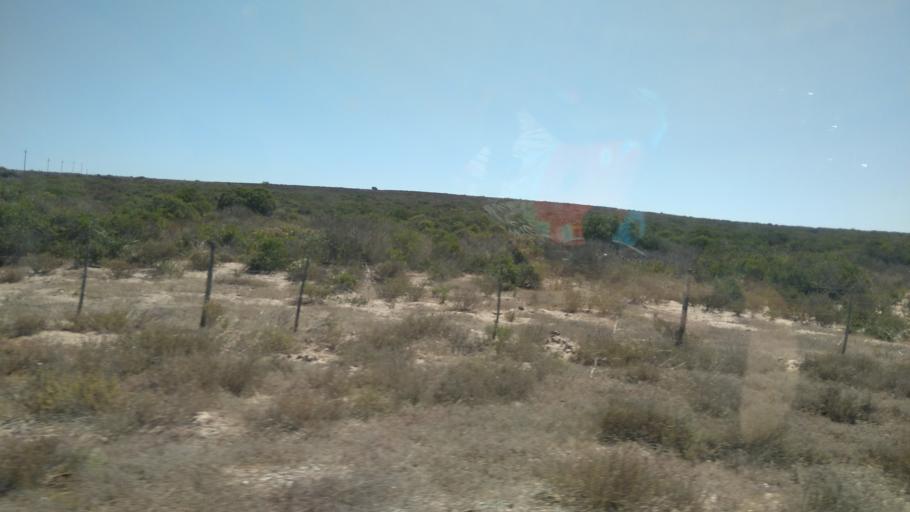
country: ZA
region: Western Cape
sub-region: West Coast District Municipality
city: Vredenburg
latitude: -33.0088
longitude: 18.1196
